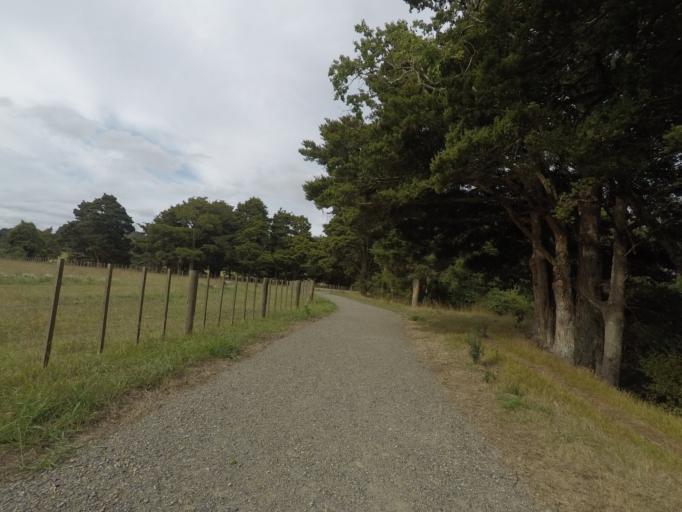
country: NZ
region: Northland
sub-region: Whangarei
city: Whangarei
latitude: -35.6778
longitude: 174.3343
